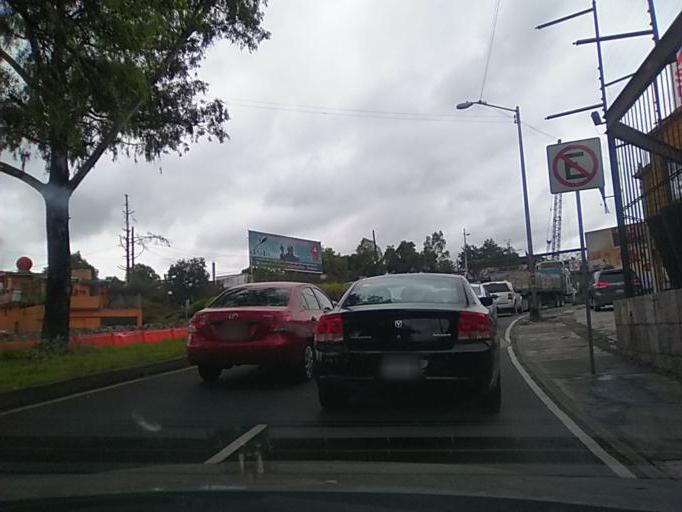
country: MX
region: Mexico City
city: Tlalpan
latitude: 19.2743
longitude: -99.1655
